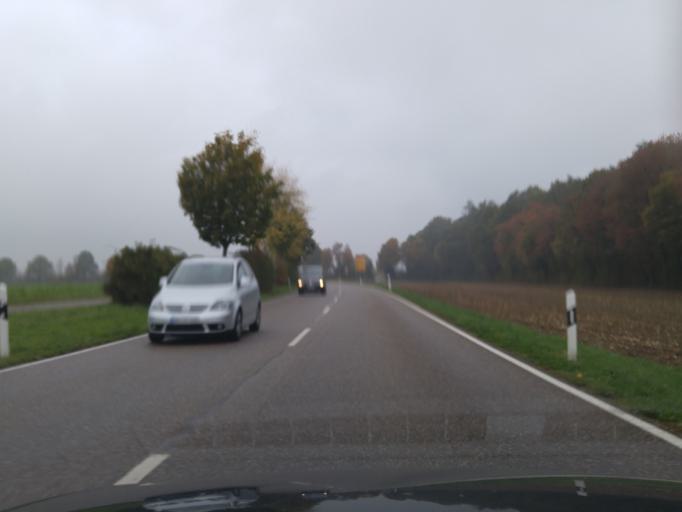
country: DE
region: Baden-Wuerttemberg
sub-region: Regierungsbezirk Stuttgart
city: Bad Rappenau
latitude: 49.2317
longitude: 9.1180
